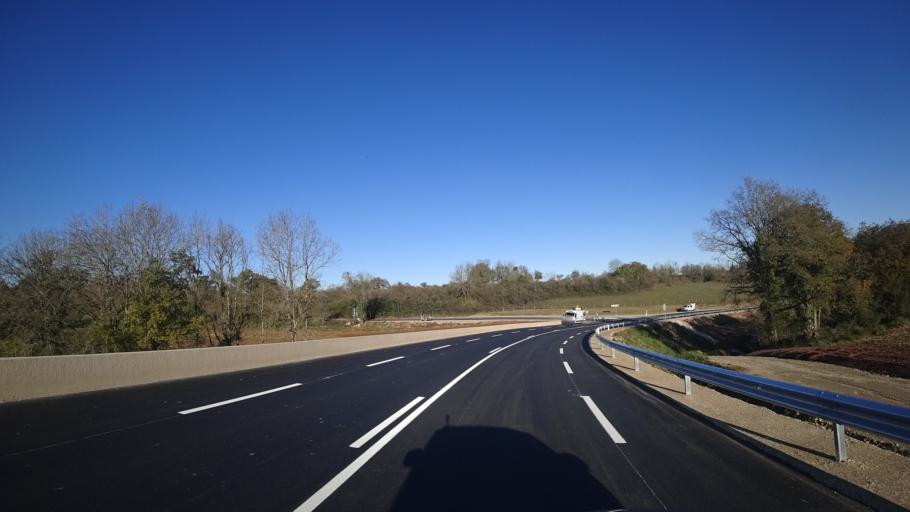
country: FR
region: Midi-Pyrenees
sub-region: Departement de l'Aveyron
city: Rodez
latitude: 44.3806
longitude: 2.5539
